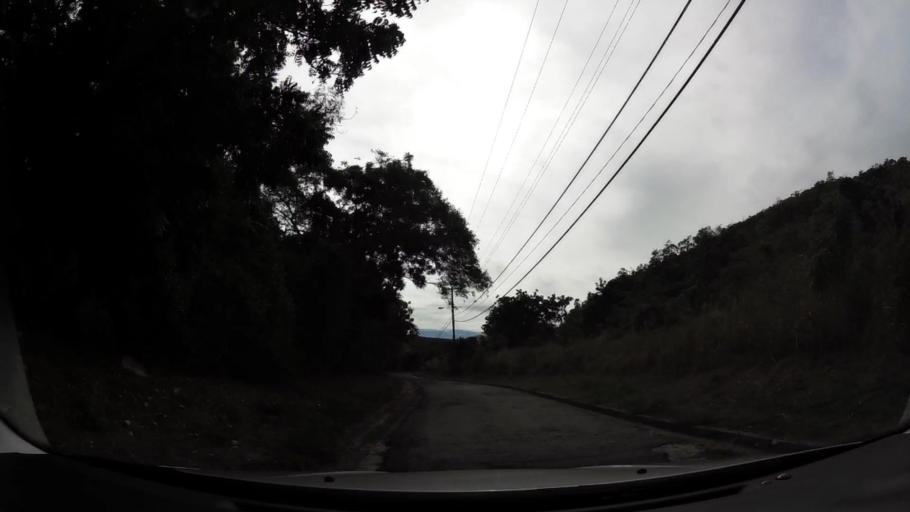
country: AG
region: Saint Peter
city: Parham
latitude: 17.0623
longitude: -61.7254
